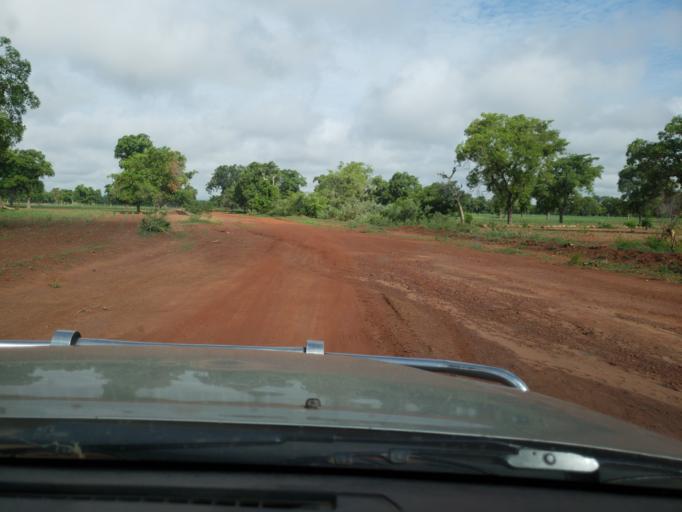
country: ML
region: Sikasso
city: Koutiala
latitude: 12.3924
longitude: -6.0101
